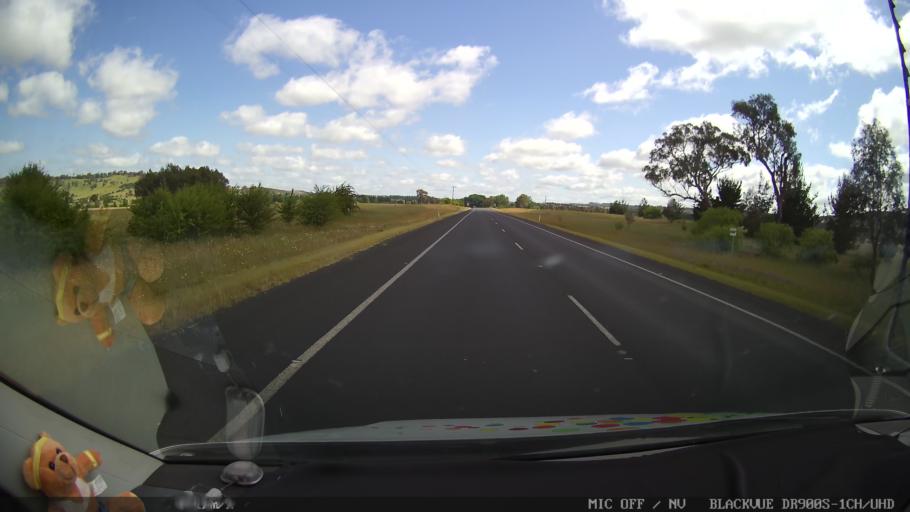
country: AU
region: New South Wales
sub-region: Glen Innes Severn
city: Glen Innes
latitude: -29.8670
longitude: 151.7368
